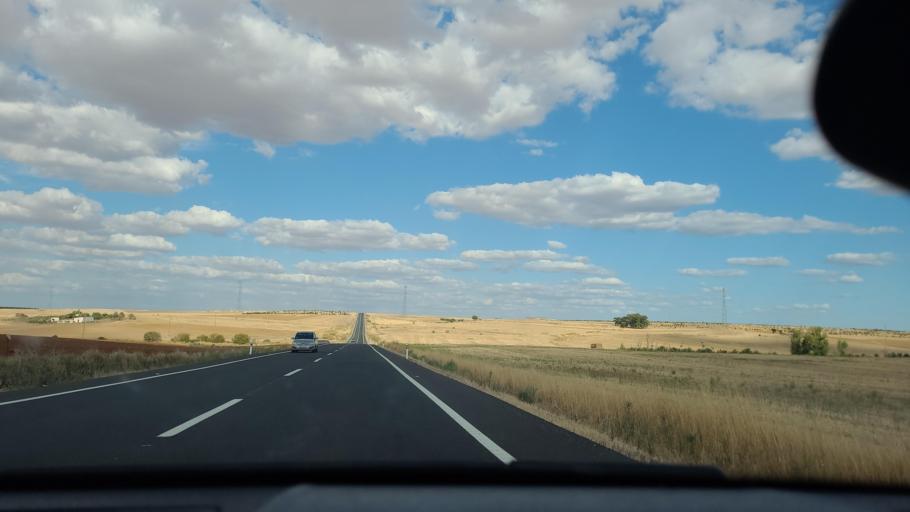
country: ES
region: Extremadura
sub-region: Provincia de Badajoz
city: Ahillones
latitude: 38.2534
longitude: -5.9177
